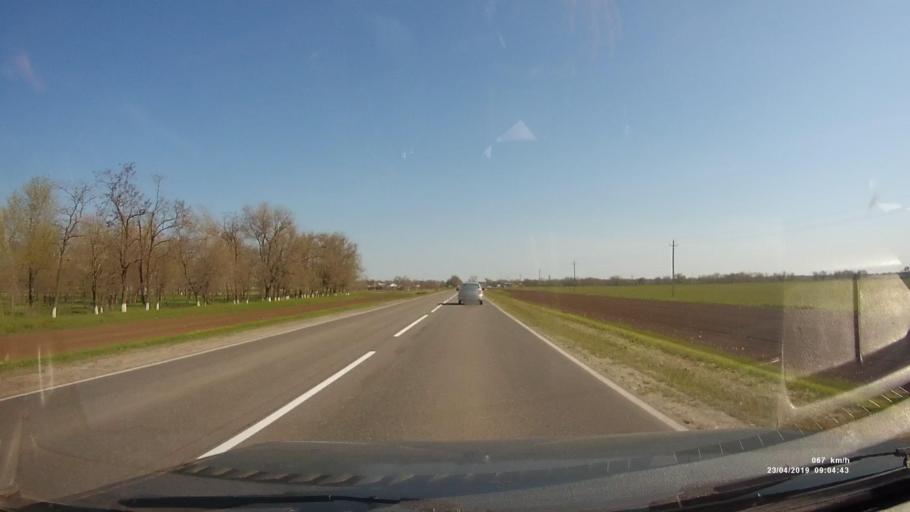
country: RU
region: Rostov
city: Sal'sk
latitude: 46.5371
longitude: 41.5821
